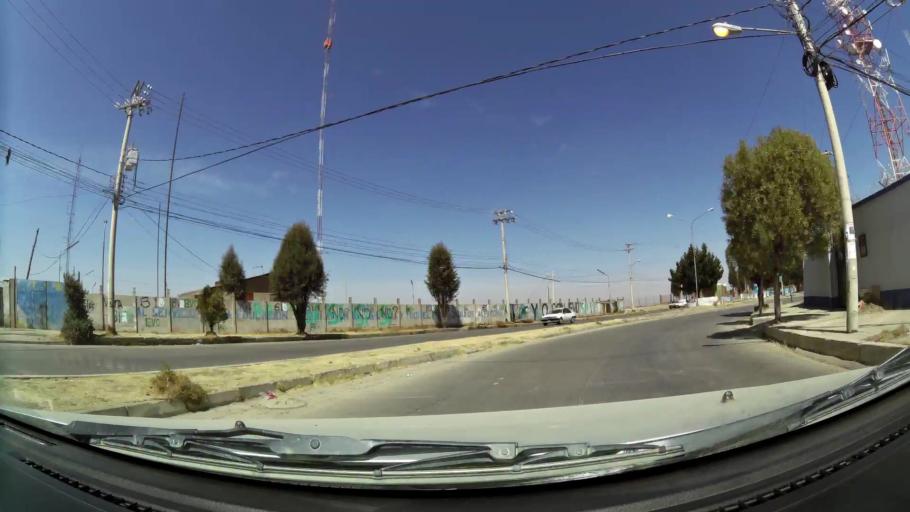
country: BO
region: La Paz
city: La Paz
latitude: -16.5285
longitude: -68.1452
